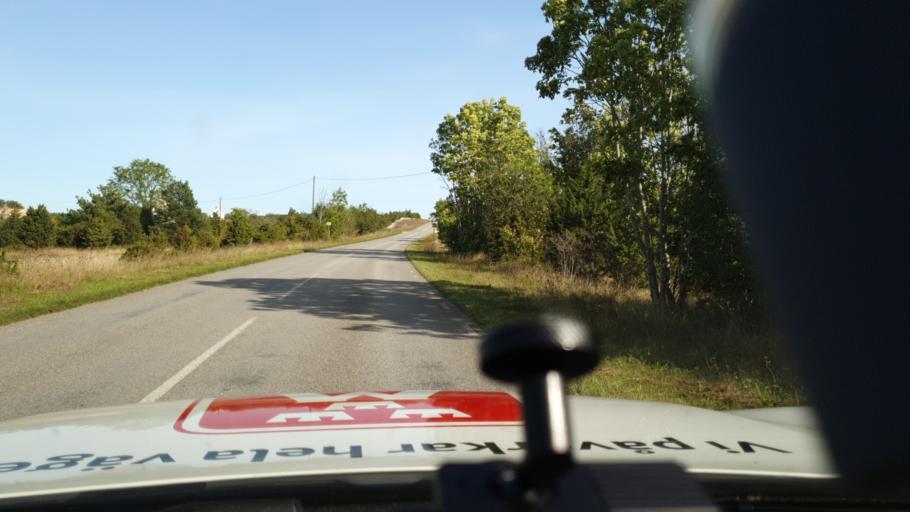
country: SE
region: Gotland
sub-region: Gotland
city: Slite
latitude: 57.9269
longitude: 19.1456
